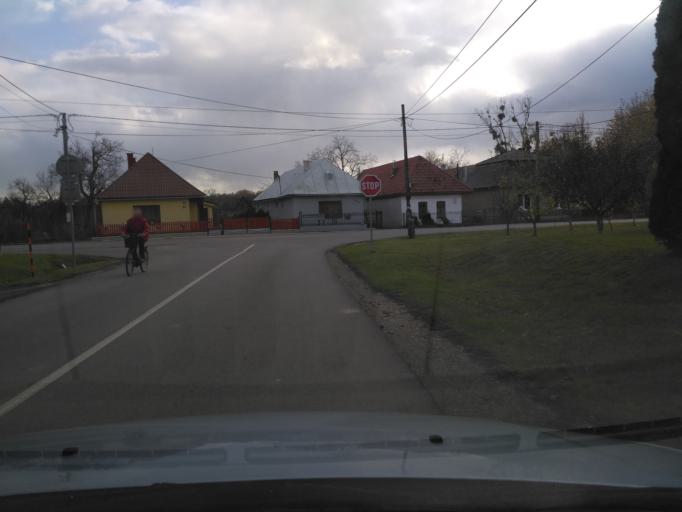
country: HU
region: Borsod-Abauj-Zemplen
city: Satoraljaujhely
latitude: 48.3959
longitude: 21.7094
